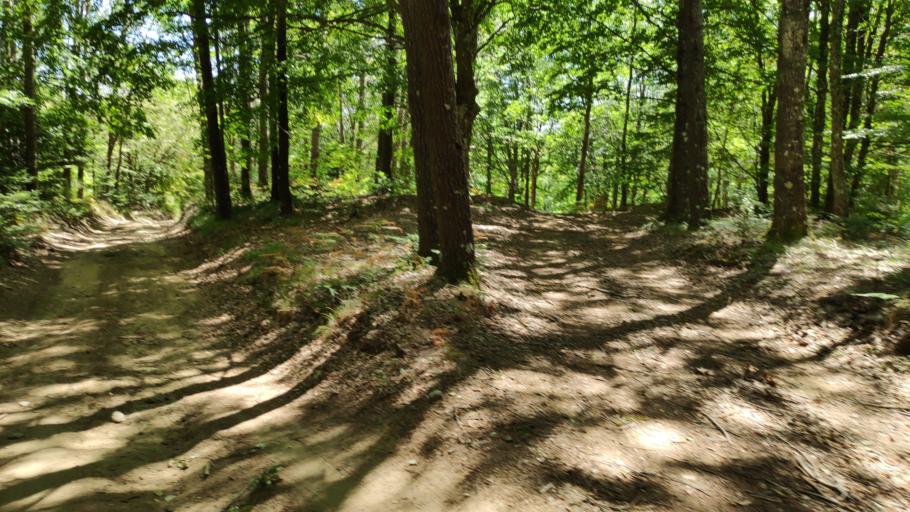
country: IT
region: Calabria
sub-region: Provincia di Vibo-Valentia
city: Mongiana
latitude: 38.5331
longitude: 16.3732
